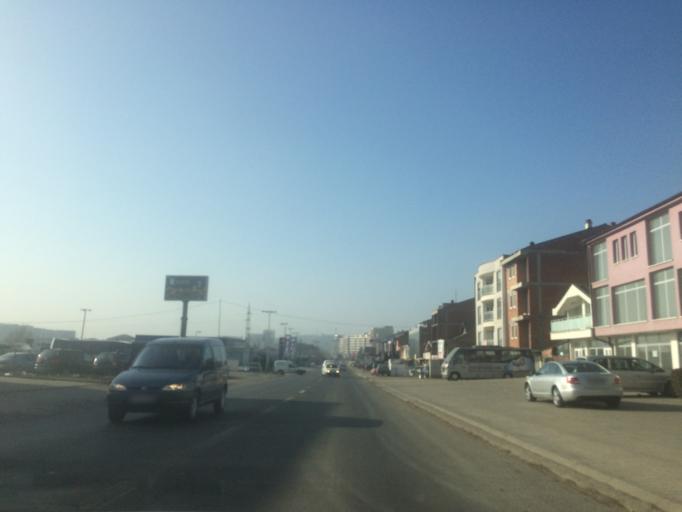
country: XK
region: Gjakova
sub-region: Komuna e Gjakoves
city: Gjakove
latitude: 42.3903
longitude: 20.4393
